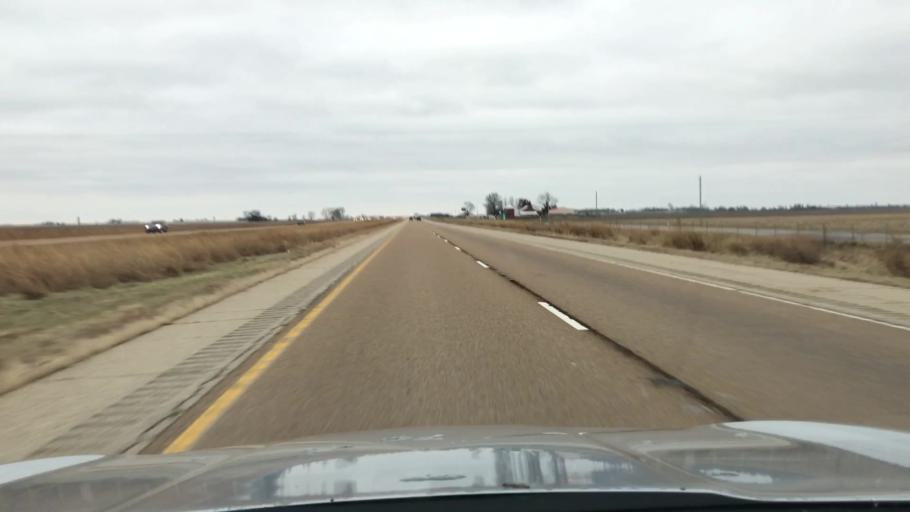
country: US
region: Illinois
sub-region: Montgomery County
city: Raymond
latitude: 39.4074
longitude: -89.6435
